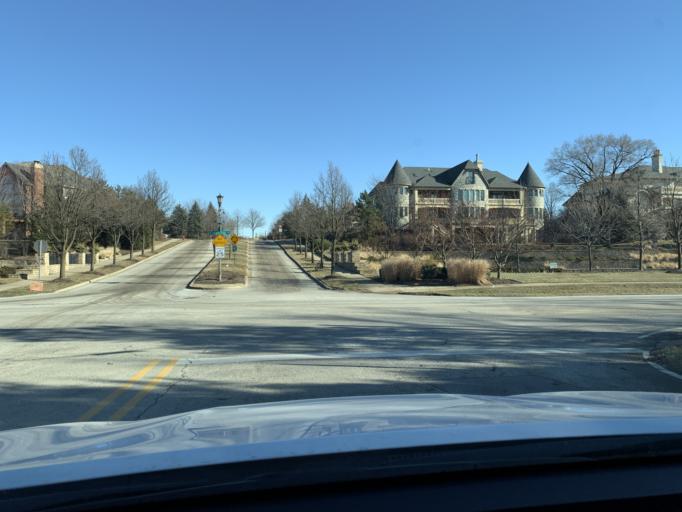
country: US
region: Illinois
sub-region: DuPage County
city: Burr Ridge
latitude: 41.7312
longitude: -87.9151
